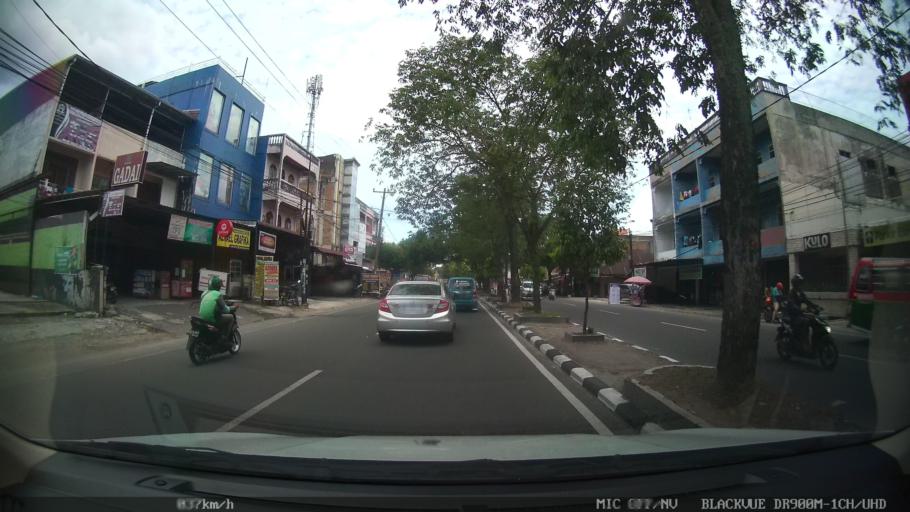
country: ID
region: North Sumatra
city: Medan
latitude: 3.5565
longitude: 98.6619
